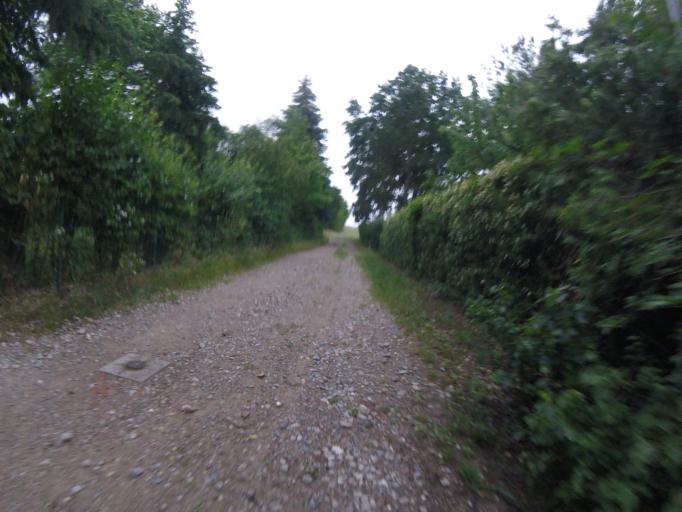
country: DE
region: Brandenburg
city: Konigs Wusterhausen
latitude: 52.2638
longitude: 13.6024
